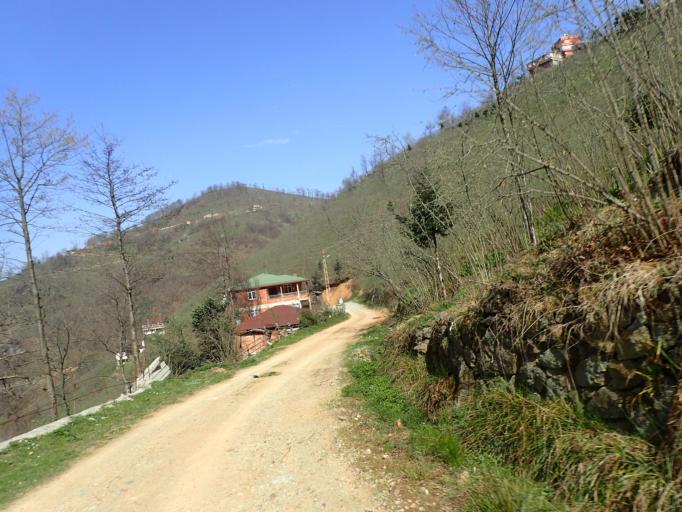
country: TR
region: Ordu
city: Kabaduz
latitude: 40.8247
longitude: 37.8767
